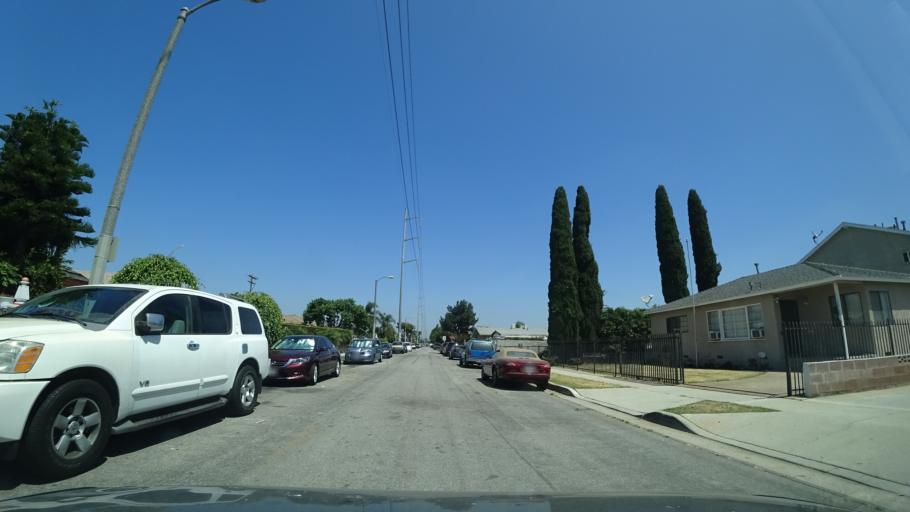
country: US
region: California
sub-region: Los Angeles County
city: Lennox
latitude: 33.9337
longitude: -118.3590
